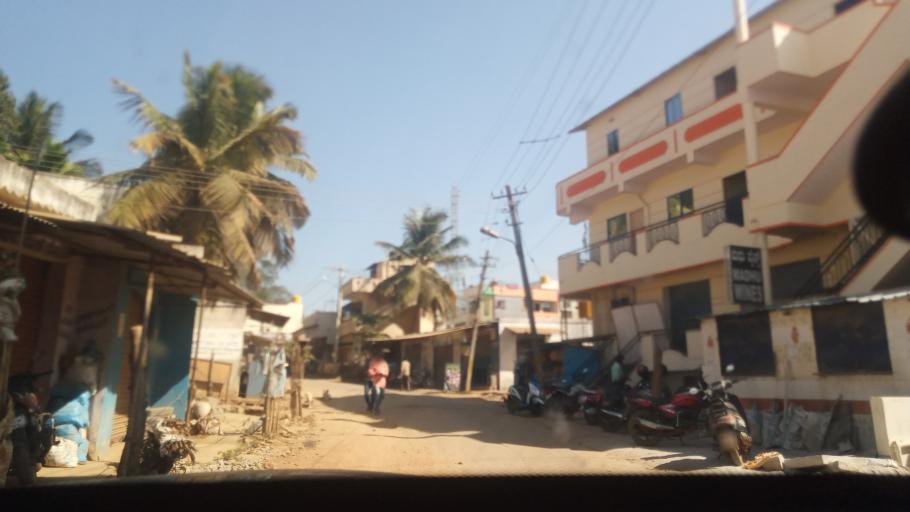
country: IN
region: Karnataka
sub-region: Bangalore Rural
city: Nelamangala
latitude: 13.0365
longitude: 77.4920
